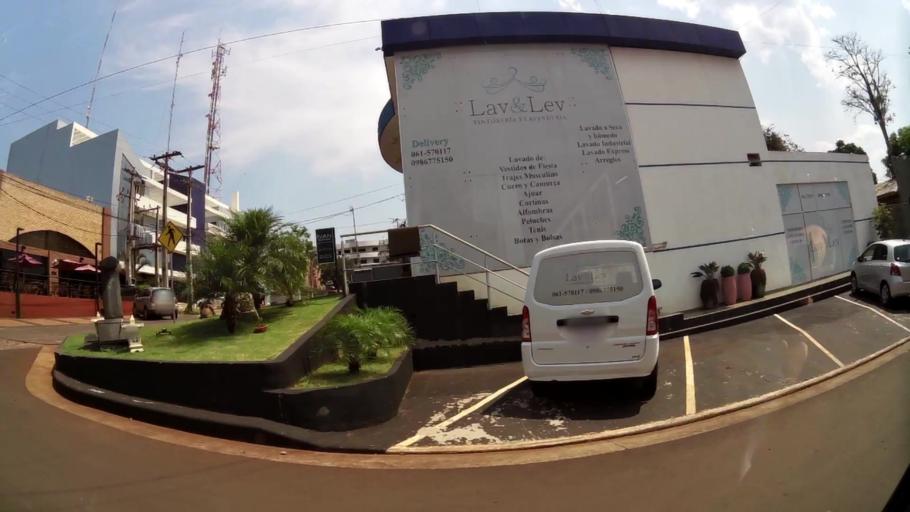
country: PY
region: Alto Parana
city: Ciudad del Este
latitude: -25.4789
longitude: -54.6232
